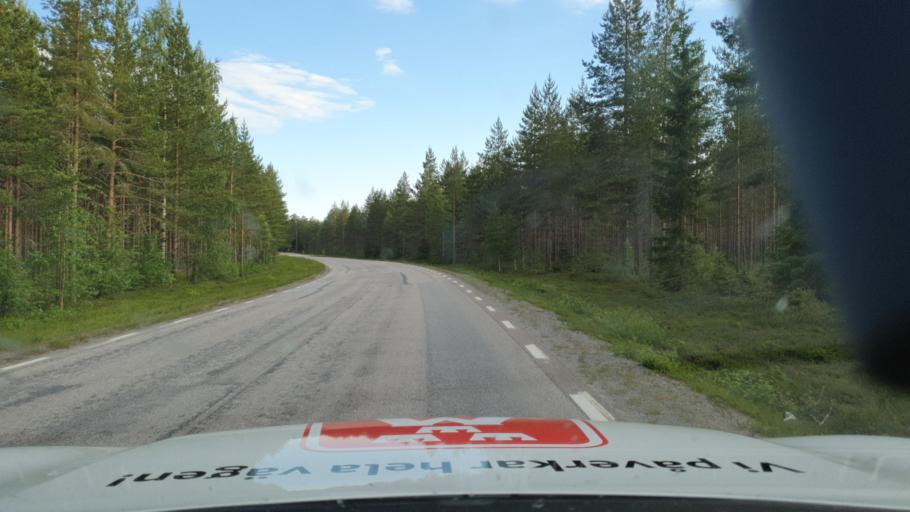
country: SE
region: Vaesterbotten
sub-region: Umea Kommun
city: Roback
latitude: 63.8615
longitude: 20.1445
